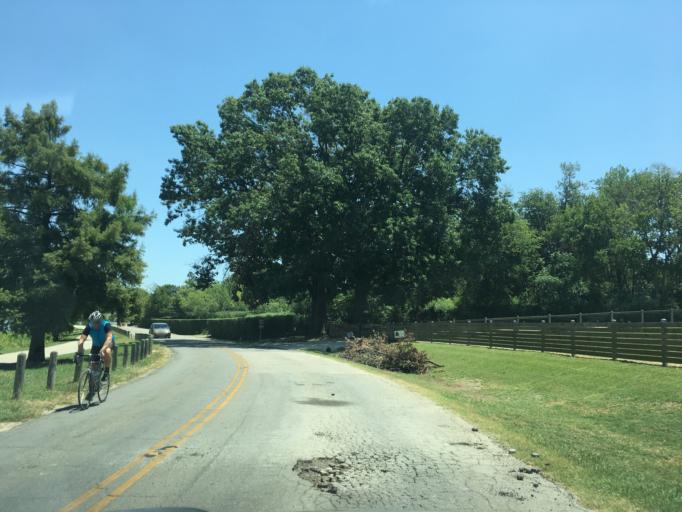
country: US
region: Texas
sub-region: Dallas County
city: Highland Park
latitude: 32.8379
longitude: -96.7270
